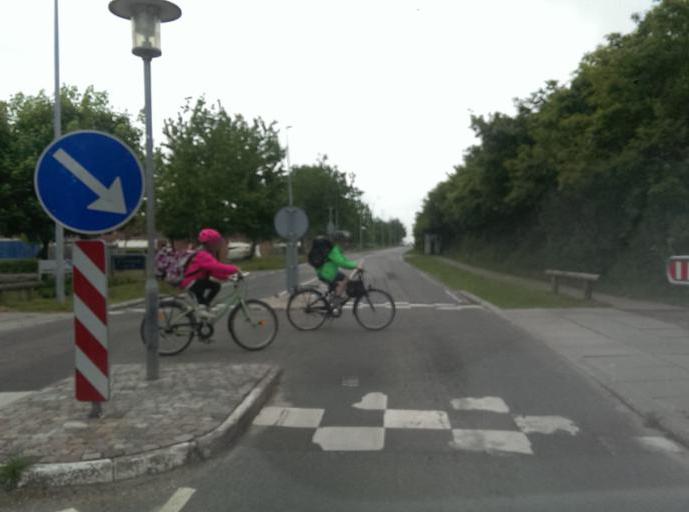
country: DK
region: South Denmark
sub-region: Fano Kommune
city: Nordby
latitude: 55.5262
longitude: 8.3653
